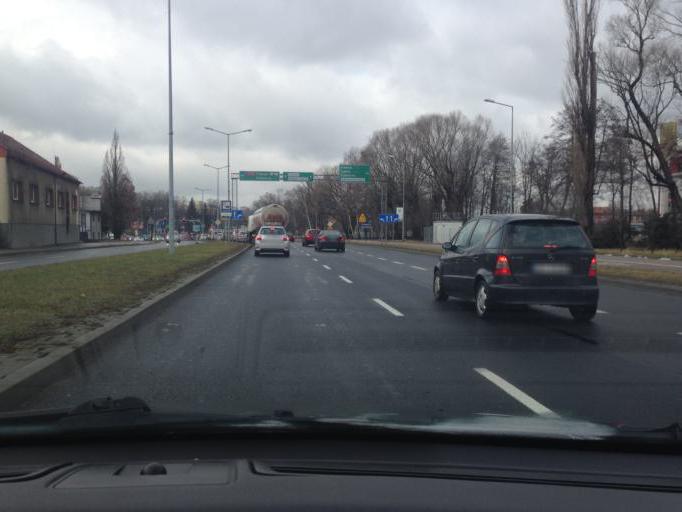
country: PL
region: Silesian Voivodeship
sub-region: Bielsko-Biala
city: Bielsko-Biala
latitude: 49.8014
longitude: 19.0490
